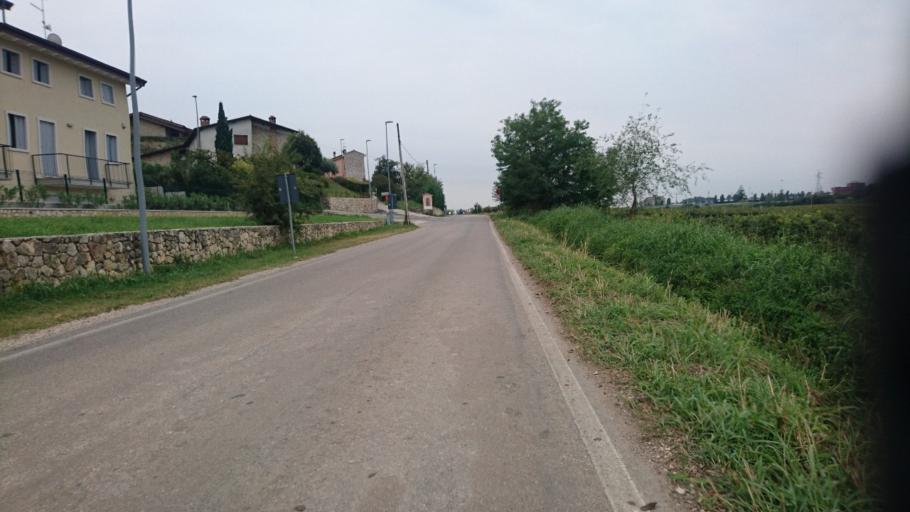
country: IT
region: Veneto
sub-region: Provincia di Verona
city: Soave
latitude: 45.4146
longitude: 11.2543
